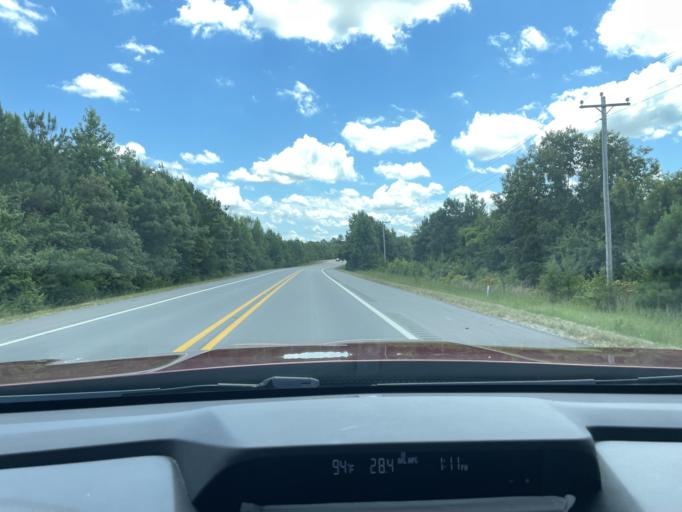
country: US
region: Arkansas
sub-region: Drew County
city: Monticello
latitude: 33.7117
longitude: -91.8094
